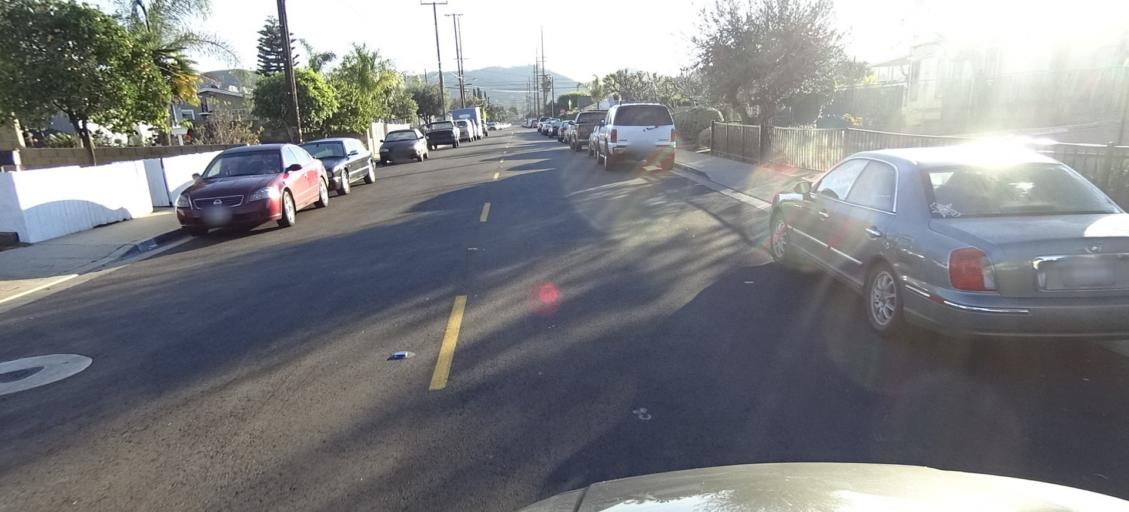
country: US
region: California
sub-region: Orange County
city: Villa Park
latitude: 33.7896
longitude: -117.8070
